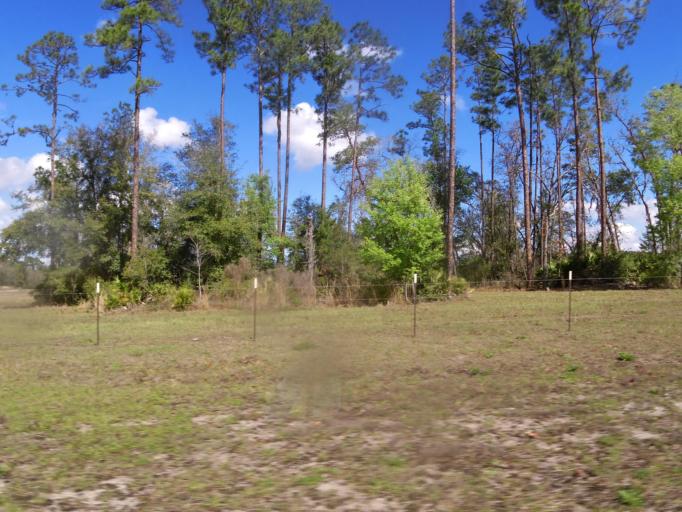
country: US
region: Florida
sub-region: Clay County
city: Green Cove Springs
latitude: 29.8681
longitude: -81.7017
